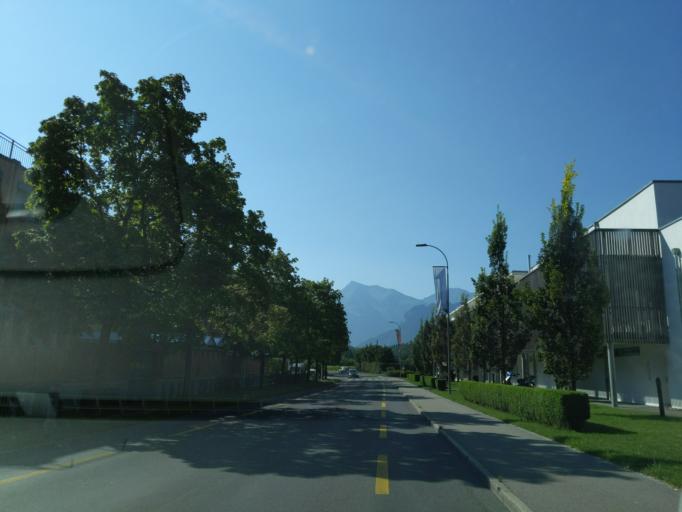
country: CH
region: Bern
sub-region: Thun District
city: Thun
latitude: 46.7403
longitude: 7.5991
